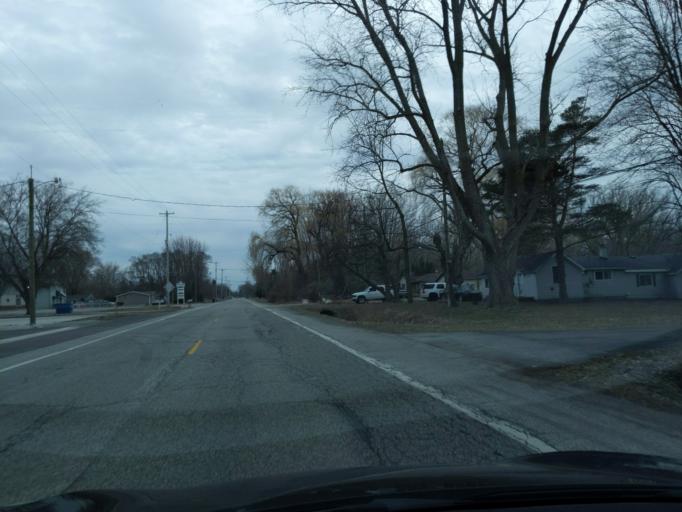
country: US
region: Michigan
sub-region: Bay County
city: Bay City
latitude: 43.6653
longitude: -83.9123
